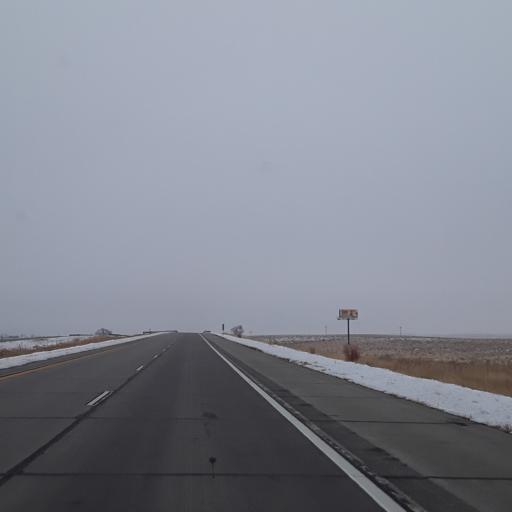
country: US
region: Colorado
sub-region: Logan County
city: Sterling
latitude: 40.5202
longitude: -103.2419
